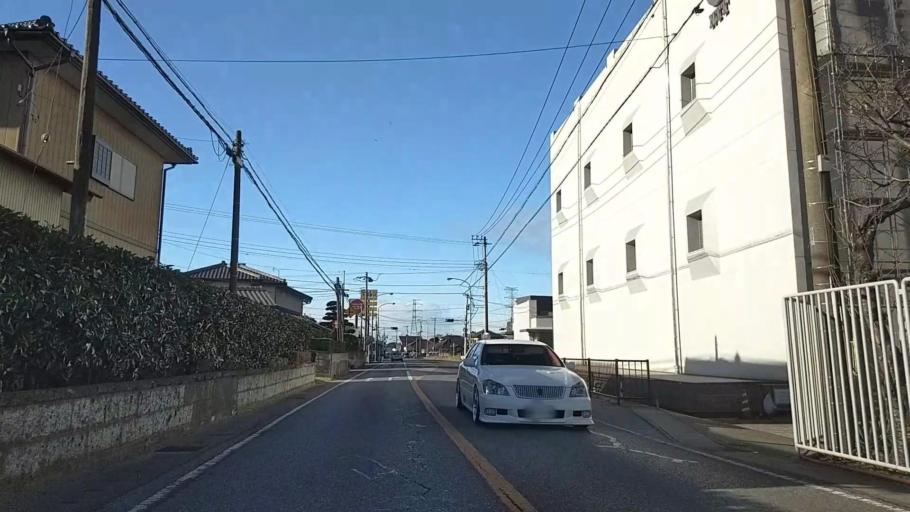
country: JP
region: Chiba
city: Futtsu
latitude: 35.3244
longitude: 139.8462
